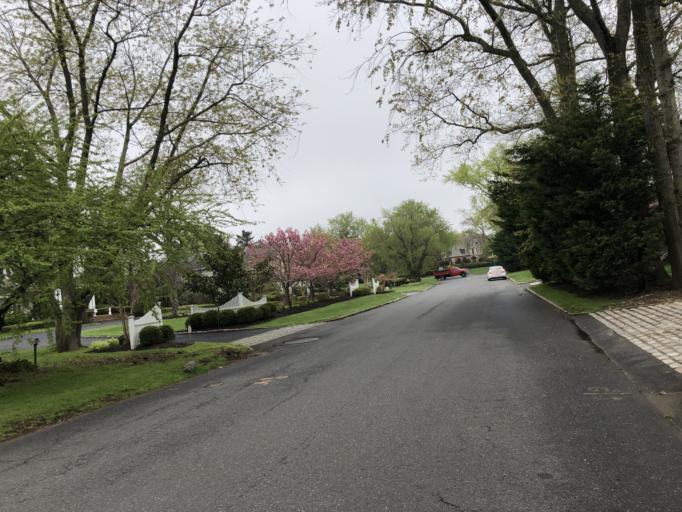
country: US
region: New York
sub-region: Nassau County
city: Hewlett
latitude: 40.6356
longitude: -73.6967
